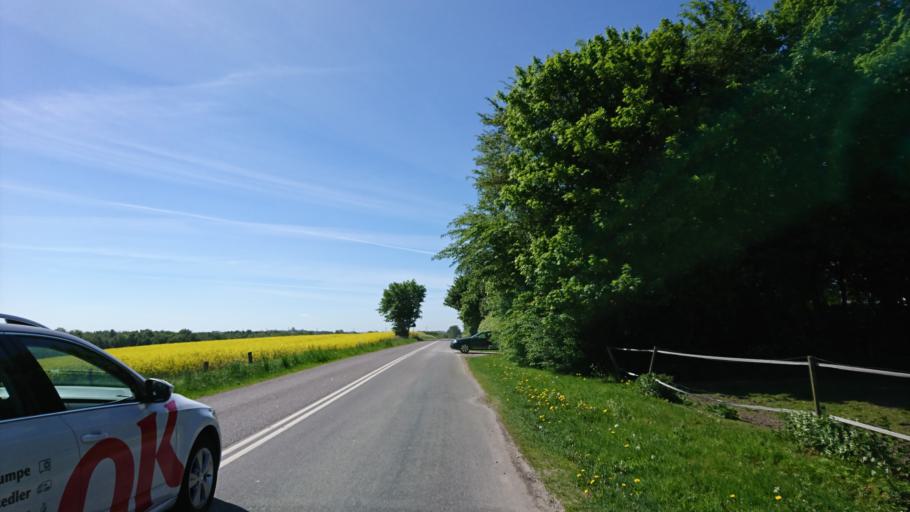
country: DK
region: Zealand
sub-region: Roskilde Kommune
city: Jyllinge
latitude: 55.7948
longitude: 12.1153
